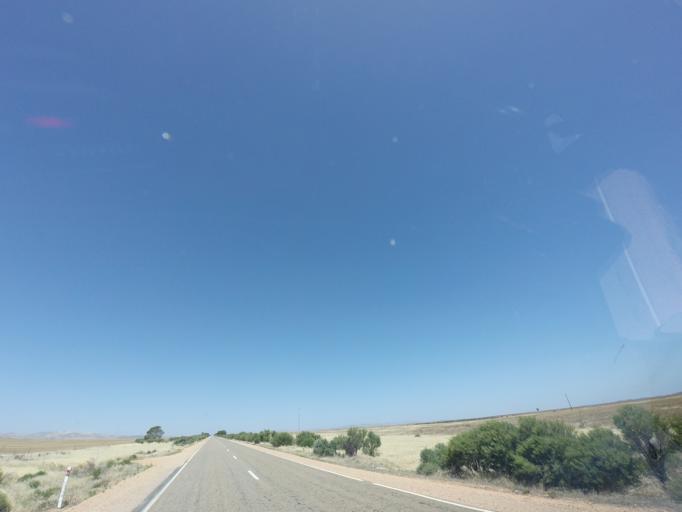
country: AU
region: South Australia
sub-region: Flinders Ranges
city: Quorn
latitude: -32.6756
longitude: 138.2766
